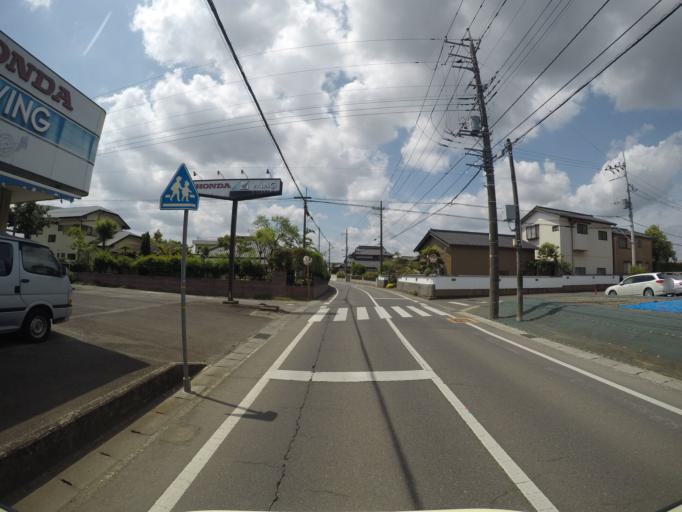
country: JP
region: Ibaraki
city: Naka
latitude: 36.0763
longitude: 140.0992
